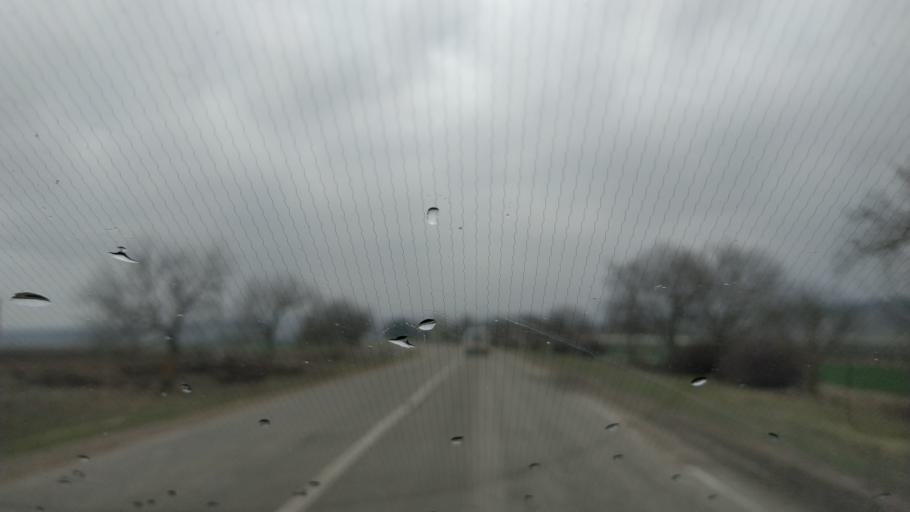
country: MD
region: Gagauzia
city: Comrat
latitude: 46.2488
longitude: 28.7596
